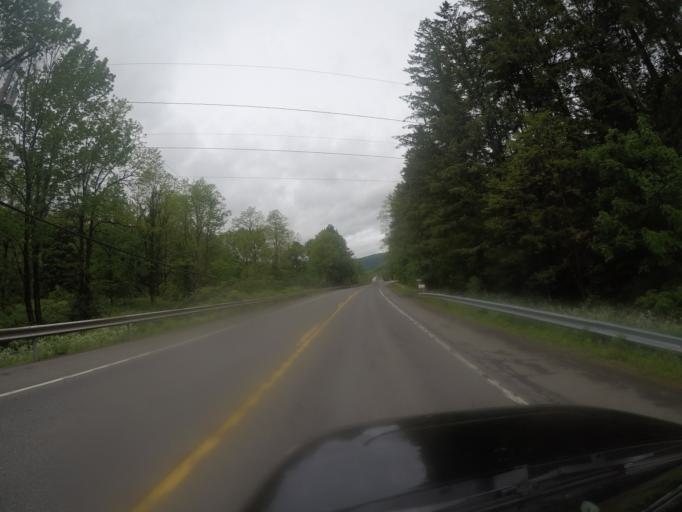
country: US
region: New York
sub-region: Ulster County
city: Shokan
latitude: 42.1152
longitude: -74.3663
